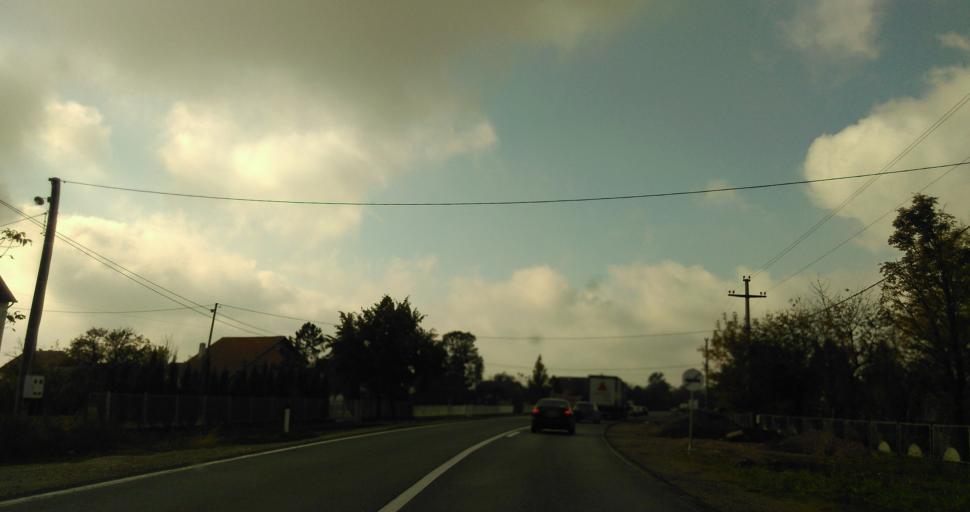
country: RS
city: Stepojevac
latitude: 44.5338
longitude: 20.2983
